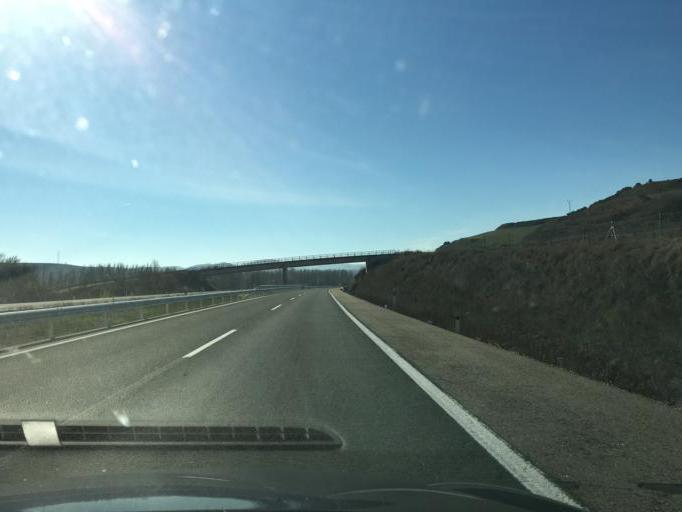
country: ES
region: Castille and Leon
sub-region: Provincia de Burgos
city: Pradanos de Bureba
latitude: 42.5043
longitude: -3.3510
